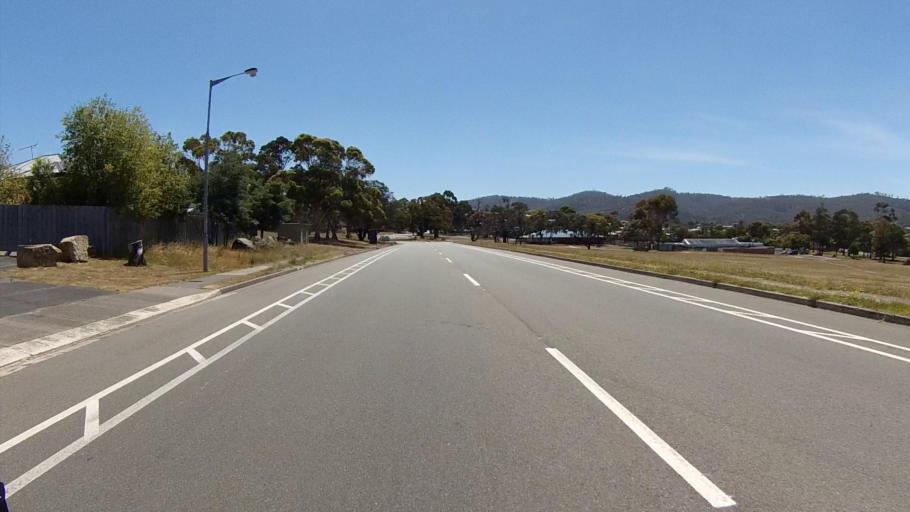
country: AU
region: Tasmania
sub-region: Clarence
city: Rokeby
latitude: -42.8985
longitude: 147.4302
